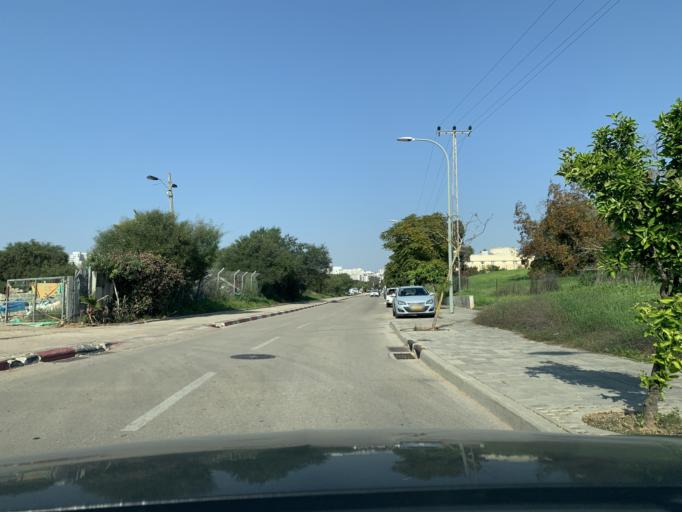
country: IL
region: Central District
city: Hod HaSharon
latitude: 32.1519
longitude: 34.8980
